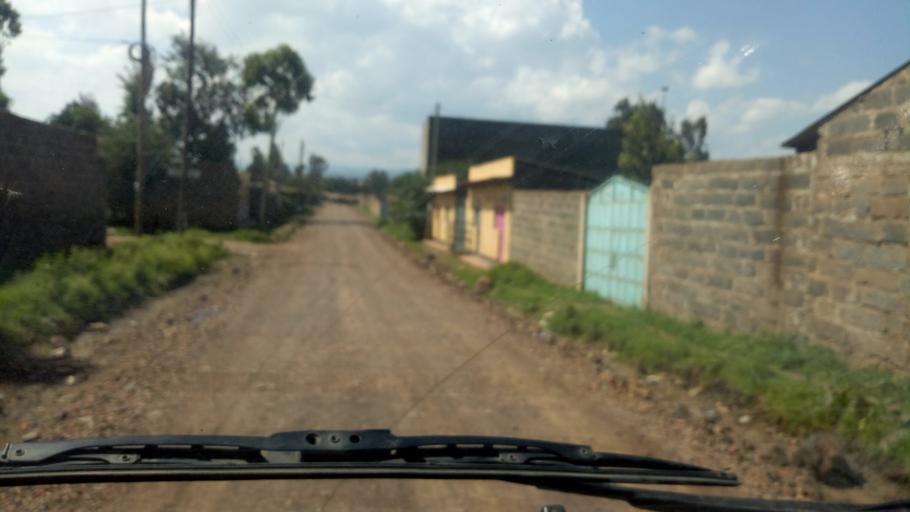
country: KE
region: Nakuru
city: Nakuru
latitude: -0.2766
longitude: 36.1102
